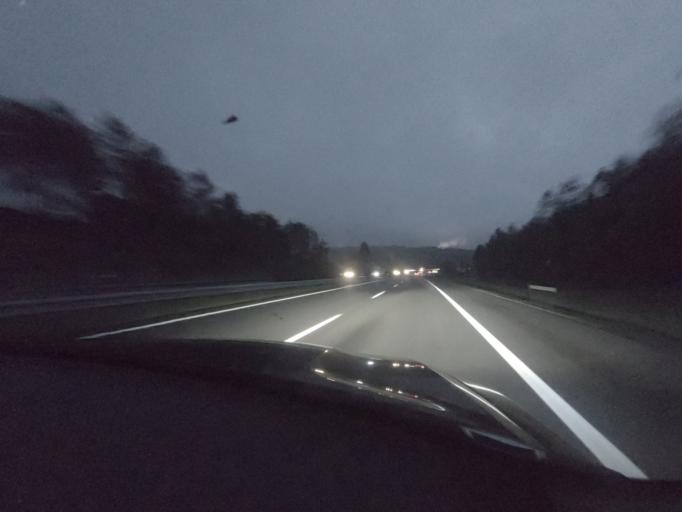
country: PT
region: Leiria
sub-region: Leiria
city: Caranguejeira
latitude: 39.8112
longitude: -8.7227
